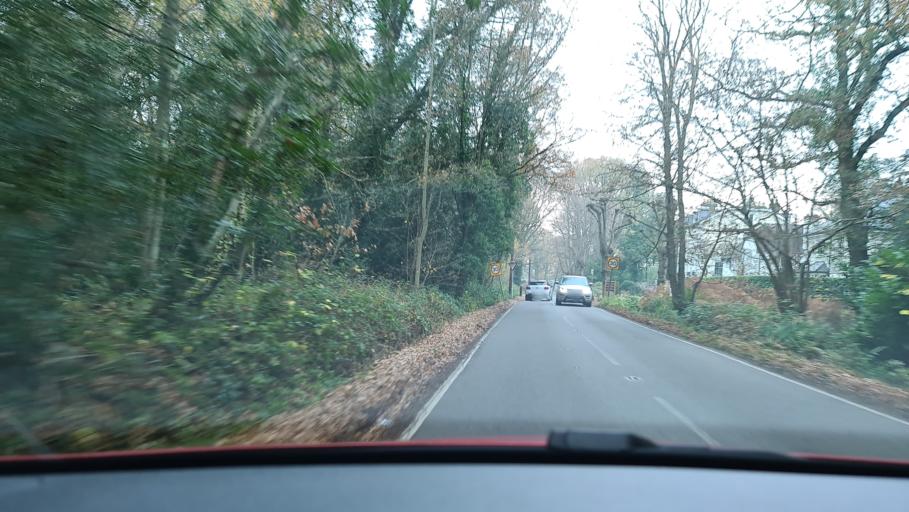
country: GB
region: England
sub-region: Surrey
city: Esher
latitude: 51.3587
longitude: -0.3838
